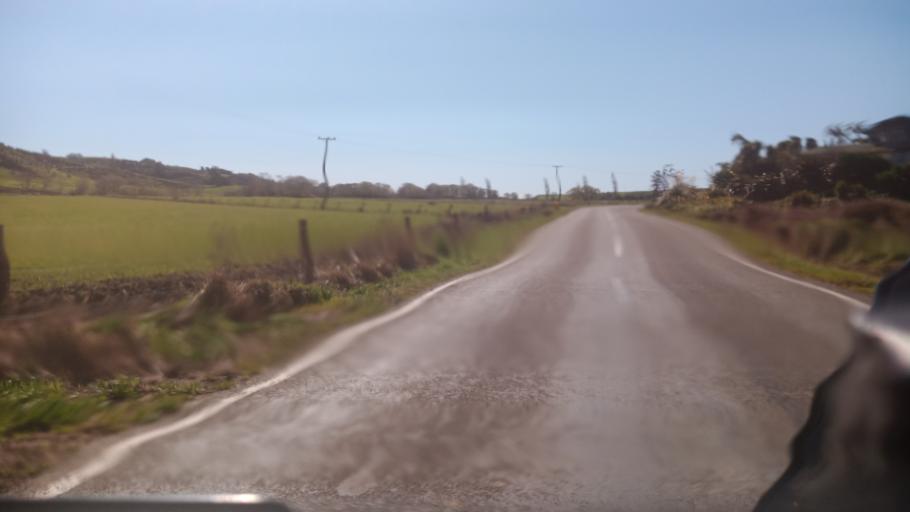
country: NZ
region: Bay of Plenty
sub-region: Opotiki District
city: Opotiki
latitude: -38.0056
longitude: 177.3960
